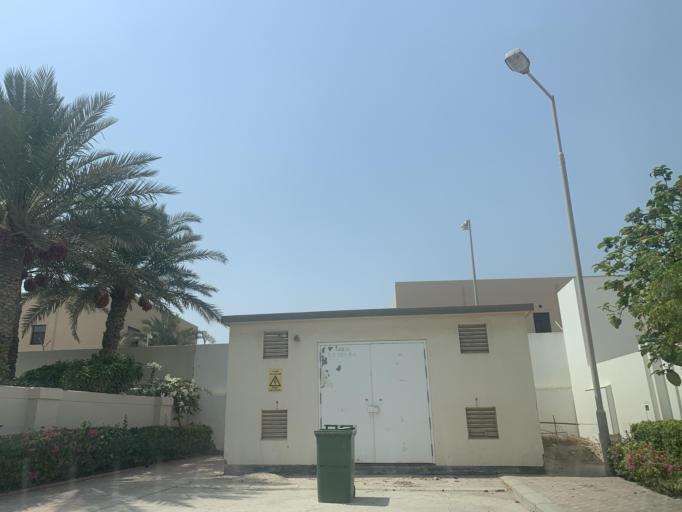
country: BH
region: Manama
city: Jidd Hafs
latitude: 26.1981
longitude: 50.4930
